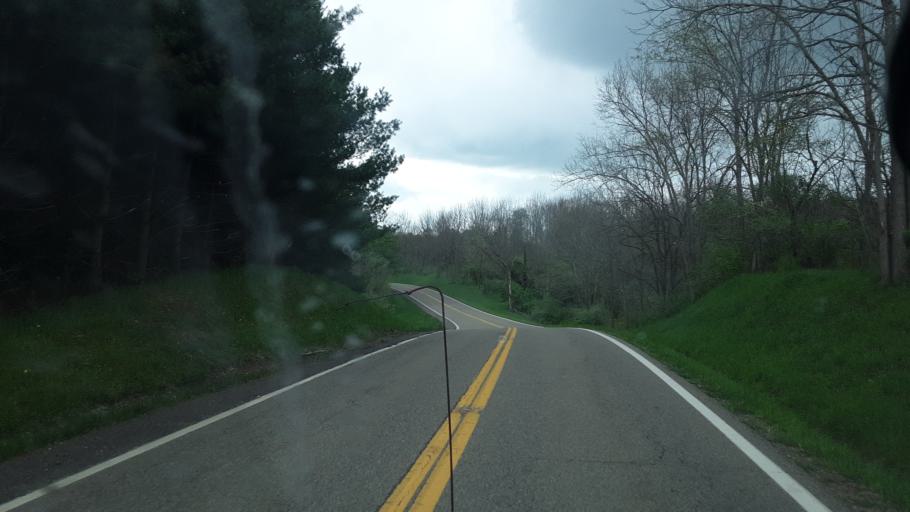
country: US
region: Ohio
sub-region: Noble County
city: Caldwell
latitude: 39.7480
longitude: -81.6222
